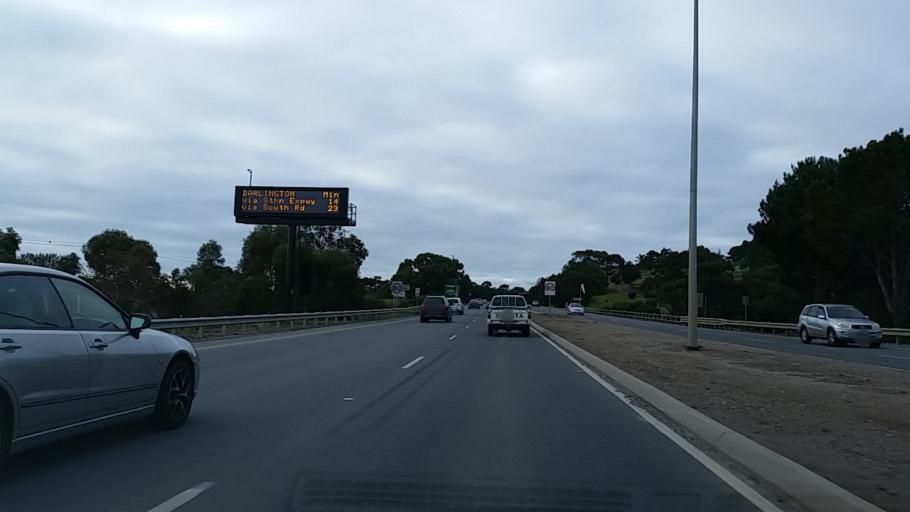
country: AU
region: South Australia
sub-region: Onkaparinga
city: Noarlunga
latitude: -35.1769
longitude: 138.4981
